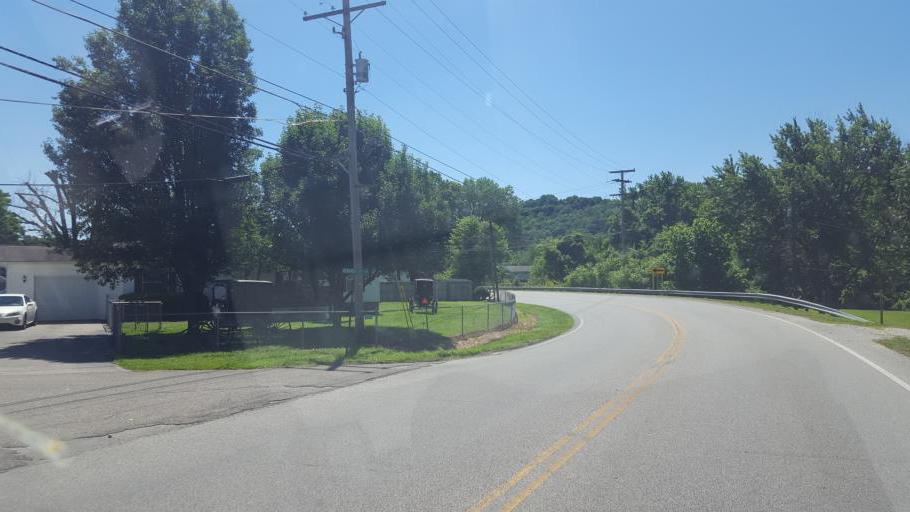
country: US
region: West Virginia
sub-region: Cabell County
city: Pea Ridge
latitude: 38.4415
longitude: -82.3539
